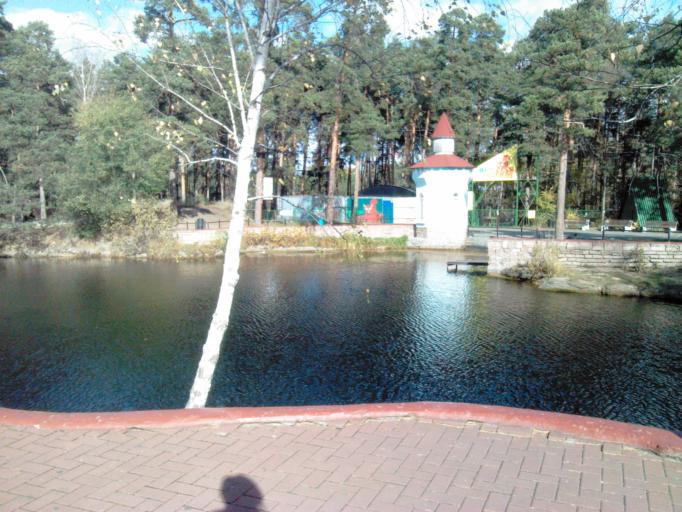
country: RU
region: Chelyabinsk
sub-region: Gorod Chelyabinsk
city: Chelyabinsk
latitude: 55.1644
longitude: 61.3654
